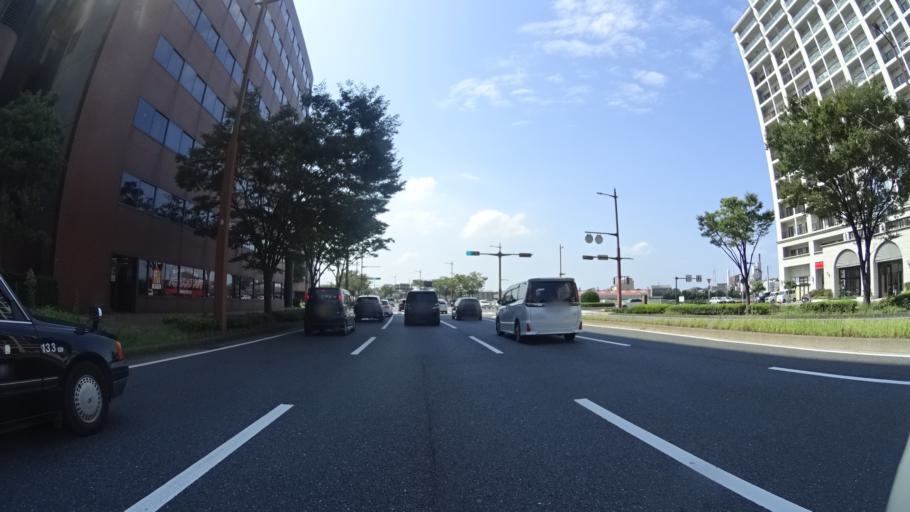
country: JP
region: Fukuoka
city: Kitakyushu
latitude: 33.8898
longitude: 130.8817
